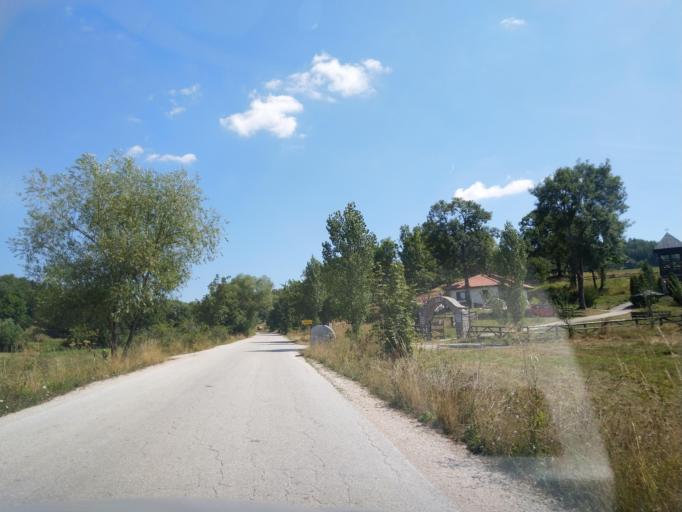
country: RS
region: Central Serbia
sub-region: Zlatiborski Okrug
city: Nova Varos
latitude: 43.4529
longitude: 19.9696
